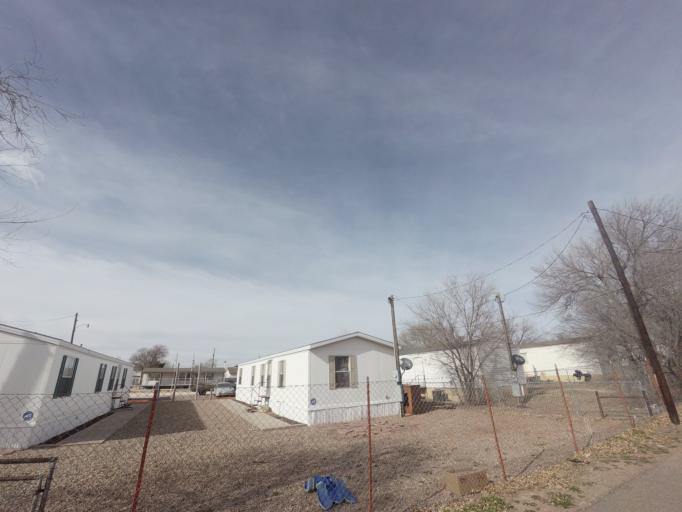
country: US
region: New Mexico
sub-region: Curry County
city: Clovis
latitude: 34.4091
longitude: -103.2337
